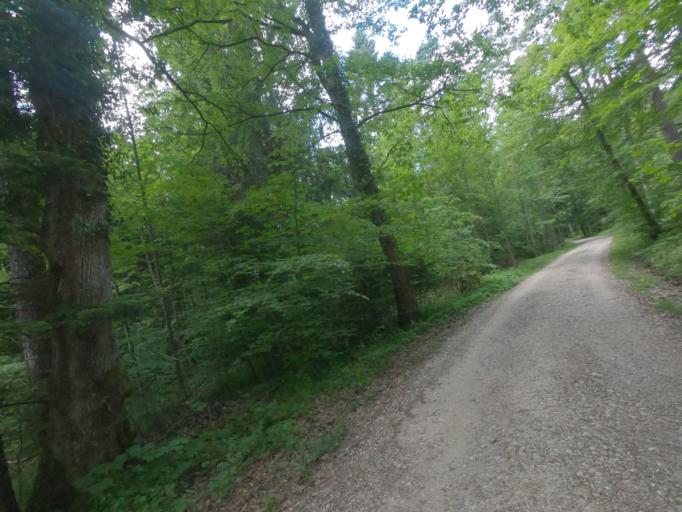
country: CH
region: Solothurn
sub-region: Bezirk Lebern
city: Riedholz
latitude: 47.2371
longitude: 7.5519
